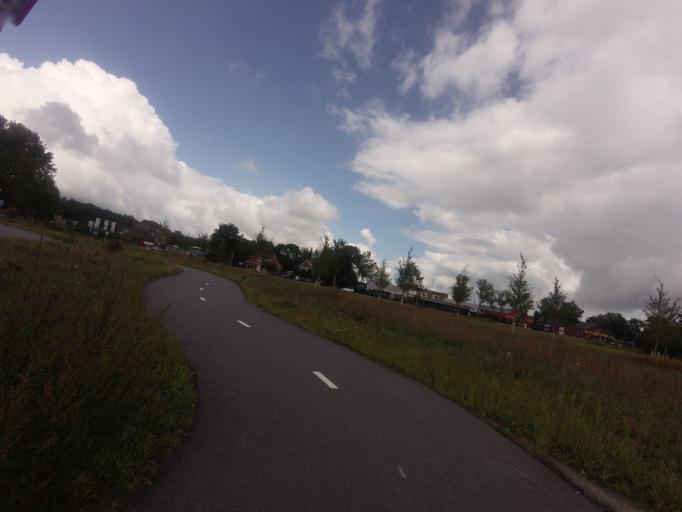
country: NL
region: Friesland
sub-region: Gemeente Skarsterlan
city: Joure
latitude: 52.9595
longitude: 5.8135
